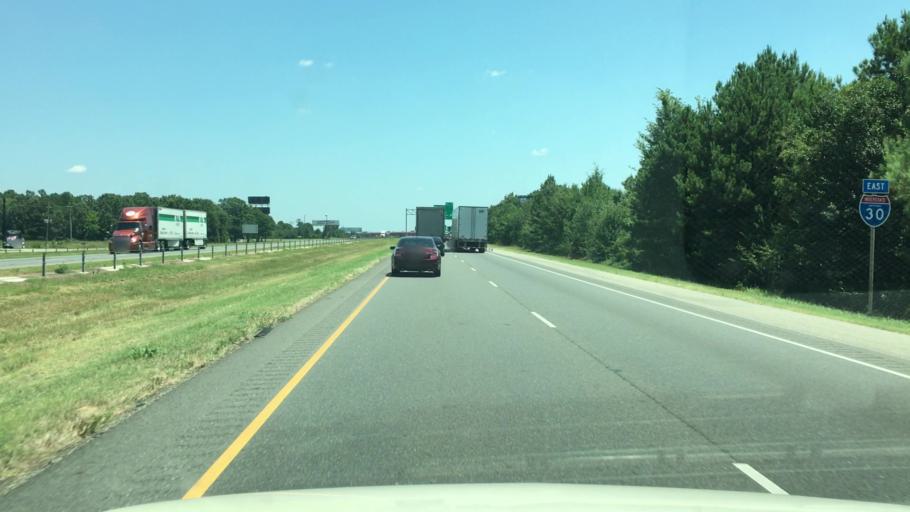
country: US
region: Arkansas
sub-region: Miller County
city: Texarkana
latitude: 33.4773
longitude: -93.9993
